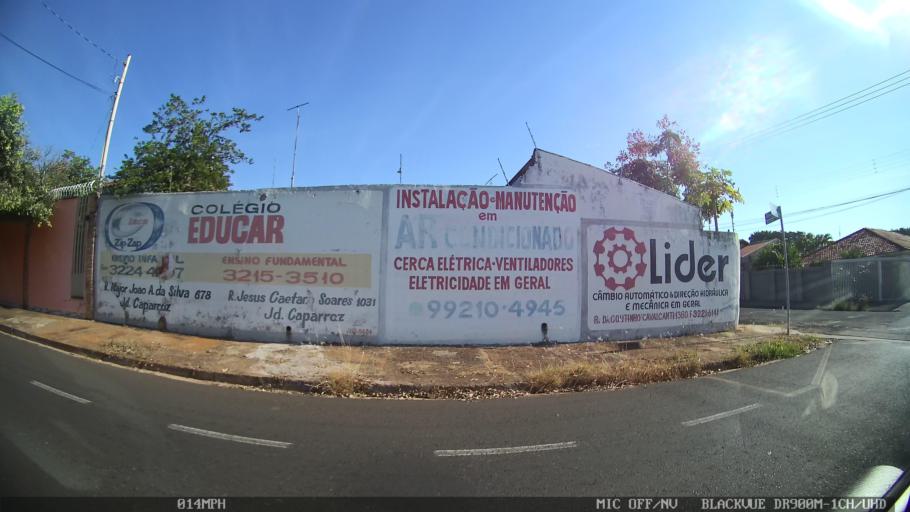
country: BR
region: Sao Paulo
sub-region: Sao Jose Do Rio Preto
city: Sao Jose do Rio Preto
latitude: -20.7810
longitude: -49.3612
